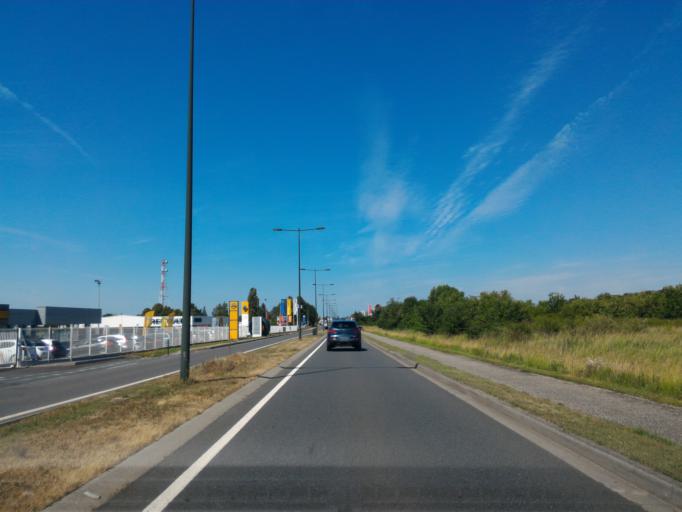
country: FR
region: Centre
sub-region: Departement de l'Indre
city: Saint-Maur
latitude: 46.7773
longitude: 1.6501
